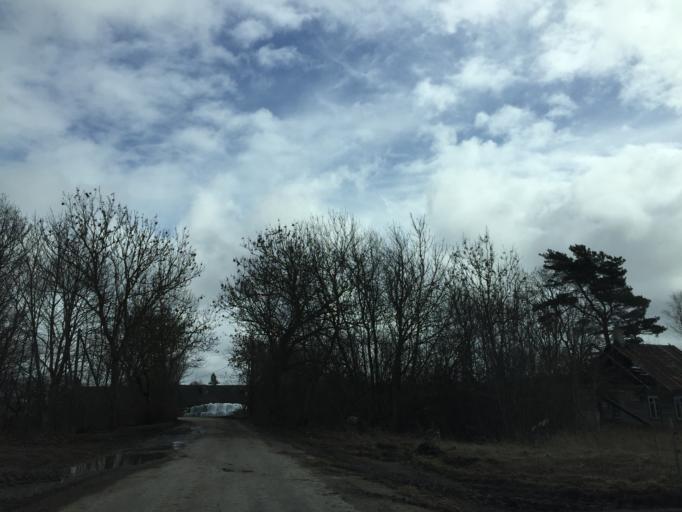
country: EE
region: Laeaene
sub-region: Lihula vald
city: Lihula
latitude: 58.7335
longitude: 23.8627
